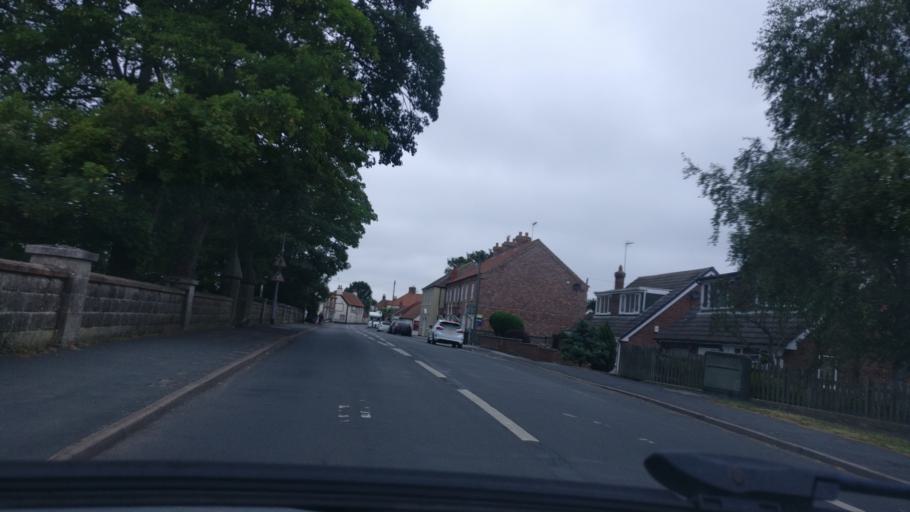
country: GB
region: England
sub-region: East Riding of Yorkshire
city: Leven
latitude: 53.8912
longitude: -0.3167
